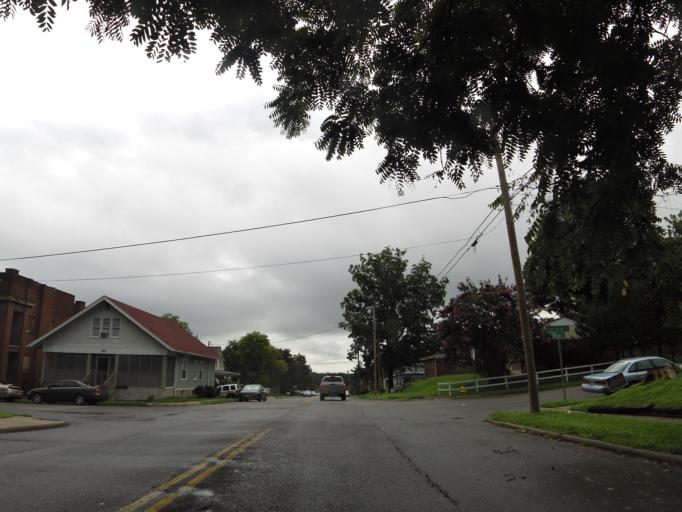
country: US
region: Missouri
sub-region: Cape Girardeau County
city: Cape Girardeau
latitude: 37.3005
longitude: -89.5219
